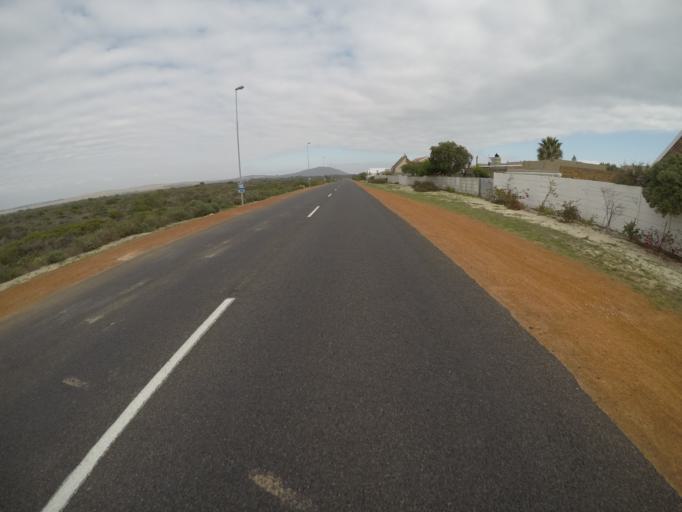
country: ZA
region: Western Cape
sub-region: City of Cape Town
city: Atlantis
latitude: -33.7019
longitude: 18.4455
